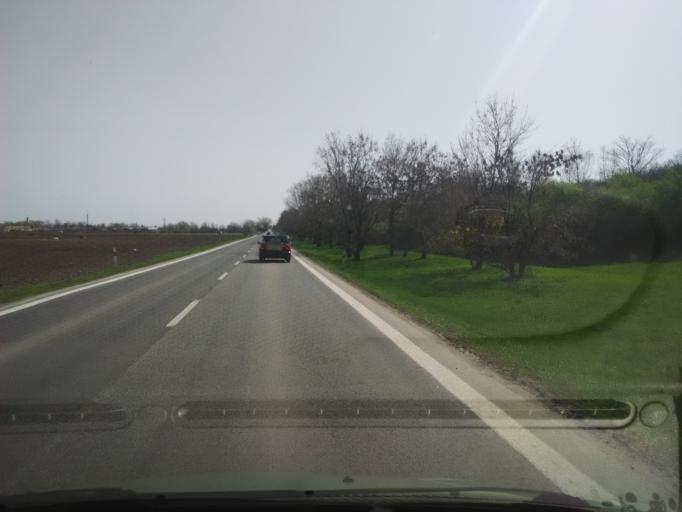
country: SK
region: Nitriansky
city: Sellye
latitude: 48.1563
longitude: 17.9131
